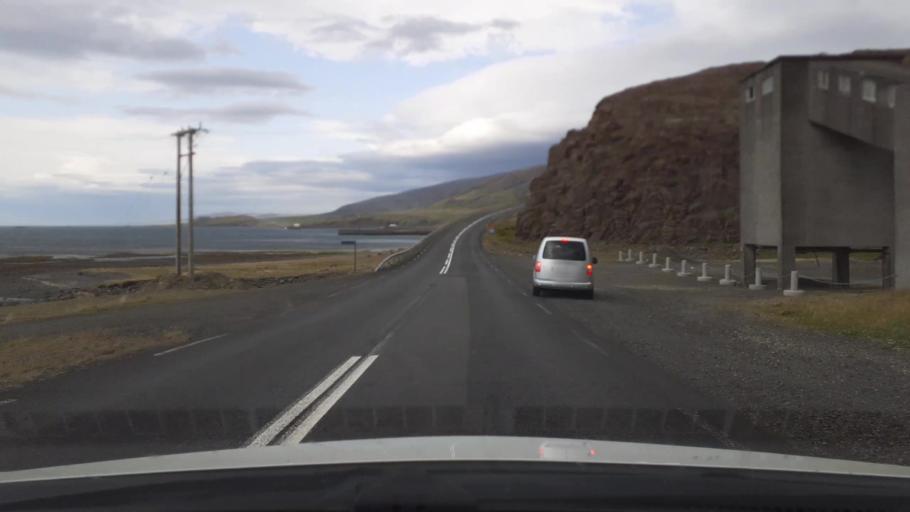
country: IS
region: Capital Region
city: Mosfellsbaer
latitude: 64.3914
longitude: -21.4293
